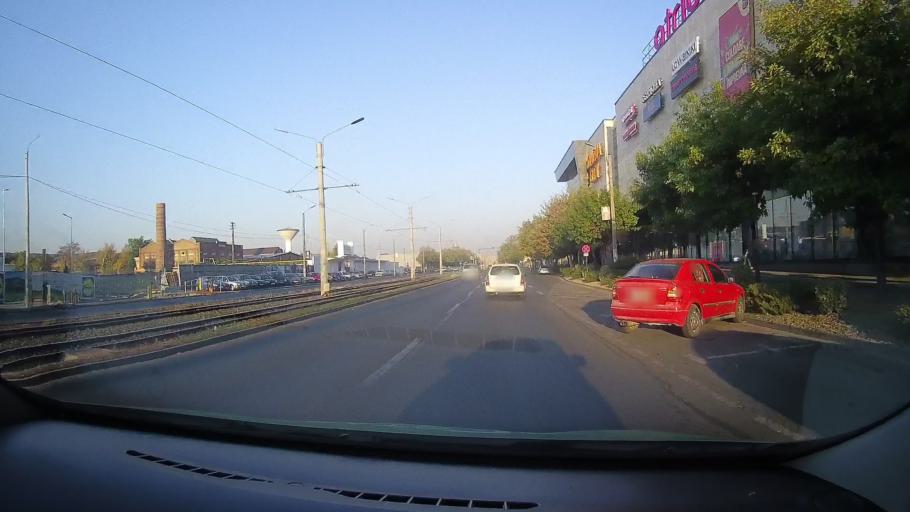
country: RO
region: Arad
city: Arad
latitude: 46.1898
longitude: 21.3206
